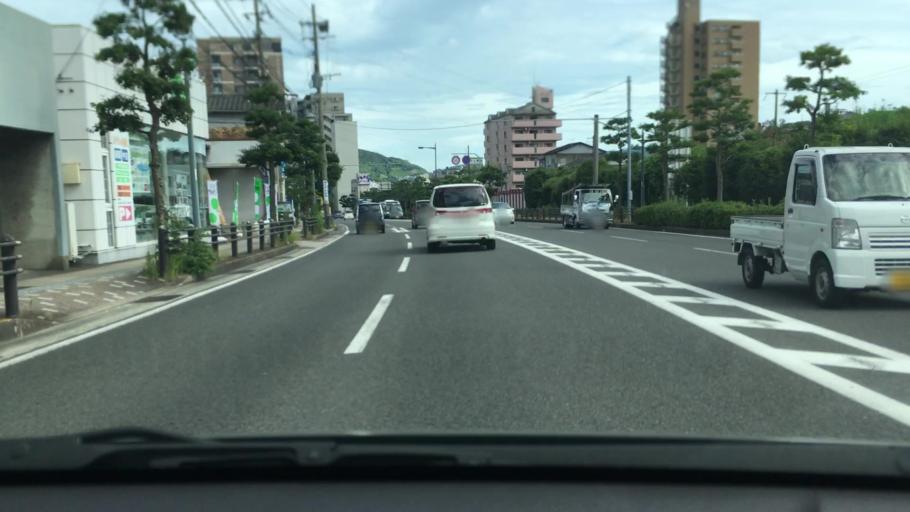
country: JP
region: Nagasaki
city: Obita
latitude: 32.7969
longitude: 129.8548
